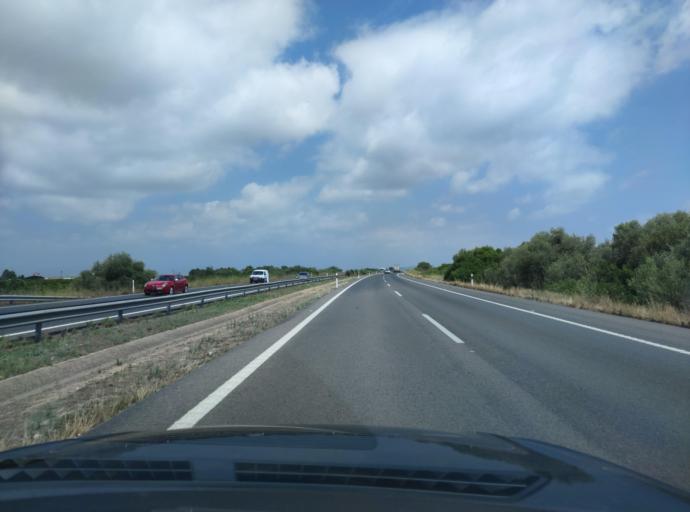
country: ES
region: Valencia
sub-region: Provincia de Castello
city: Vinaros
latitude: 40.4917
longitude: 0.4152
